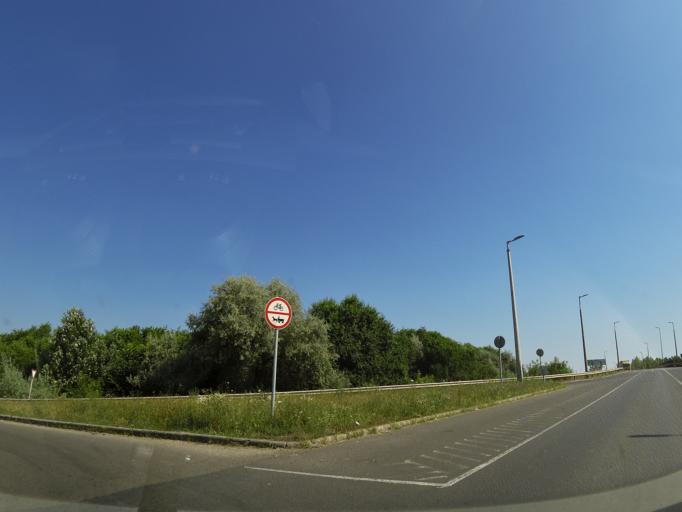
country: HU
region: Jasz-Nagykun-Szolnok
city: Toszeg
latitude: 47.1441
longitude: 20.1608
